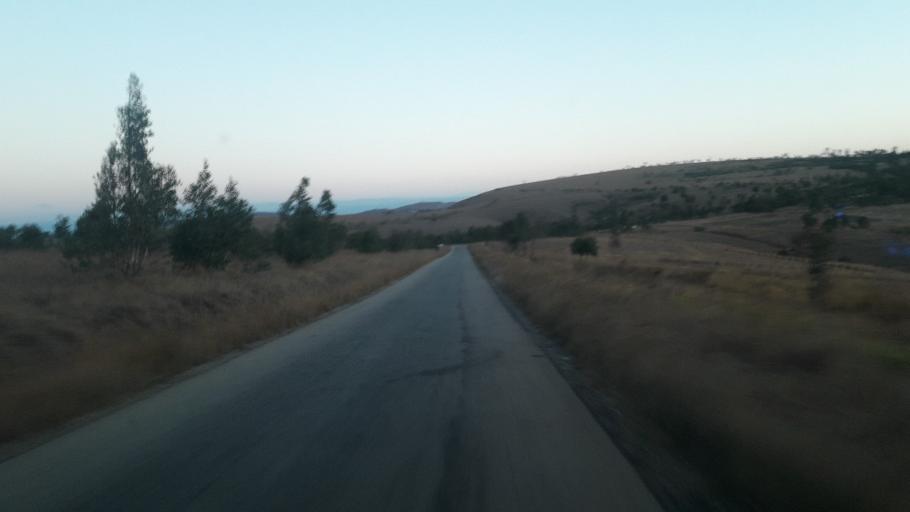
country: MG
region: Analamanga
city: Ankazobe
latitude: -18.4669
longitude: 47.1675
